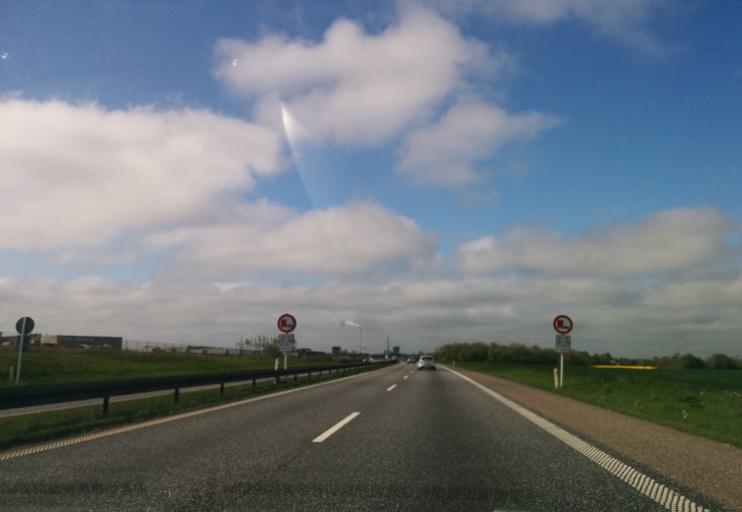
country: DK
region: Central Jutland
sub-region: Hedensted Kommune
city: Hedensted
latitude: 55.8136
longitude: 9.6816
